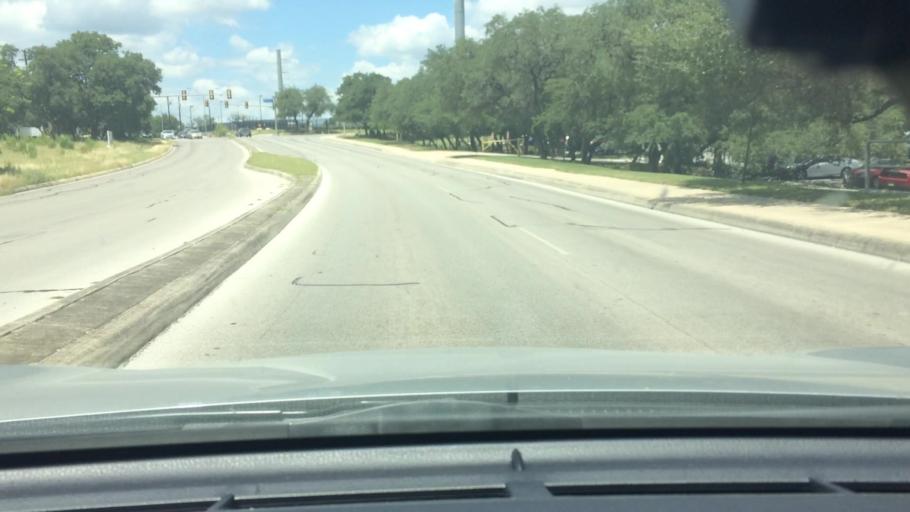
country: US
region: Texas
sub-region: Bexar County
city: Leon Valley
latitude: 29.4758
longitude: -98.6932
